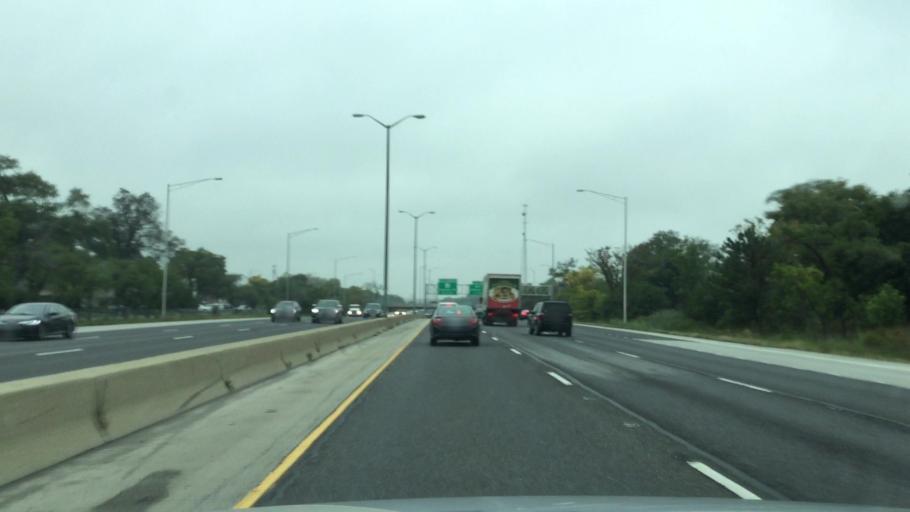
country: US
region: Illinois
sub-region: Cook County
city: Northfield
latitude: 42.0985
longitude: -87.7657
